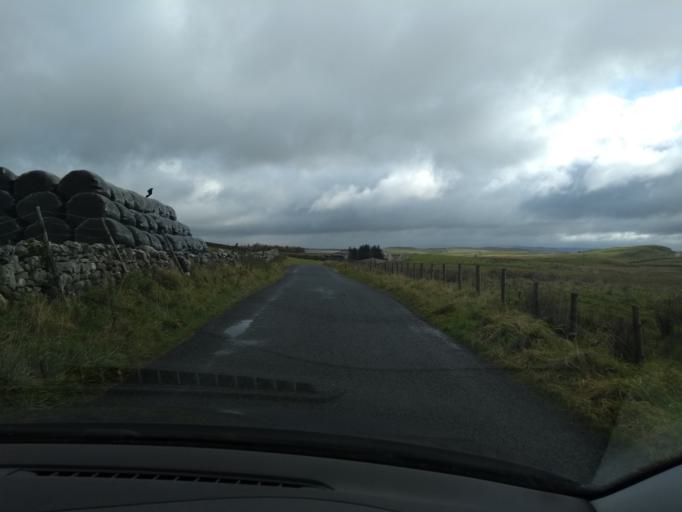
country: GB
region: England
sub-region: North Yorkshire
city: Settle
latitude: 54.0954
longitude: -2.1951
